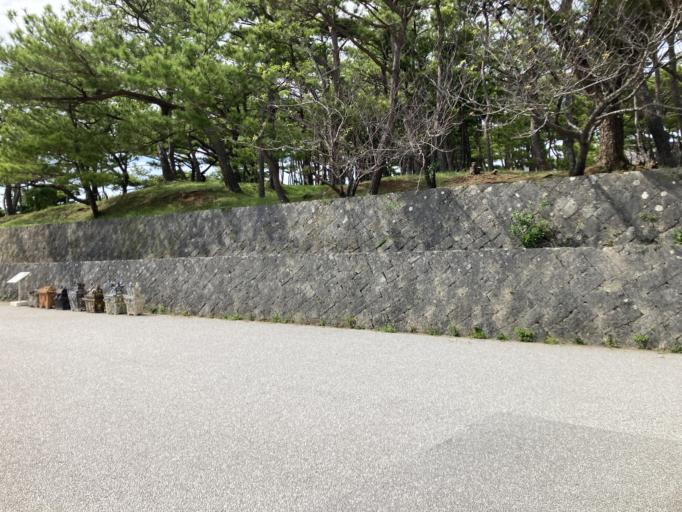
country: JP
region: Okinawa
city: Ishikawa
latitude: 26.4070
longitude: 127.7425
